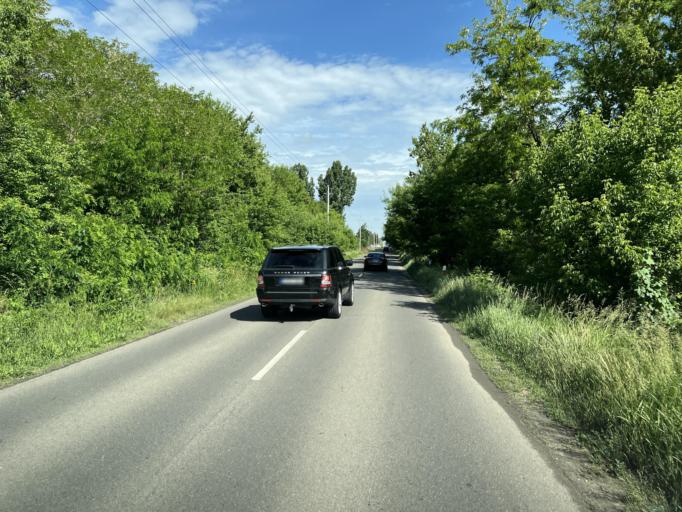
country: HU
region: Pest
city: Isaszeg
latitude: 47.5619
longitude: 19.3769
